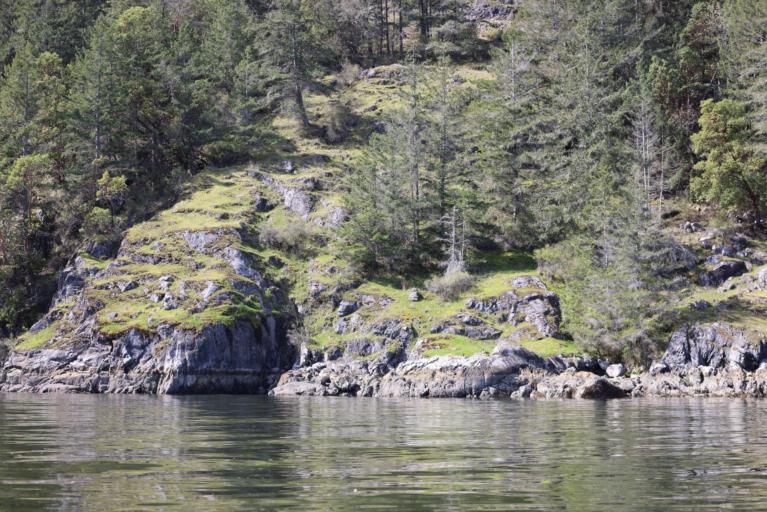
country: CA
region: British Columbia
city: Langford
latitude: 48.5790
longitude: -123.5185
